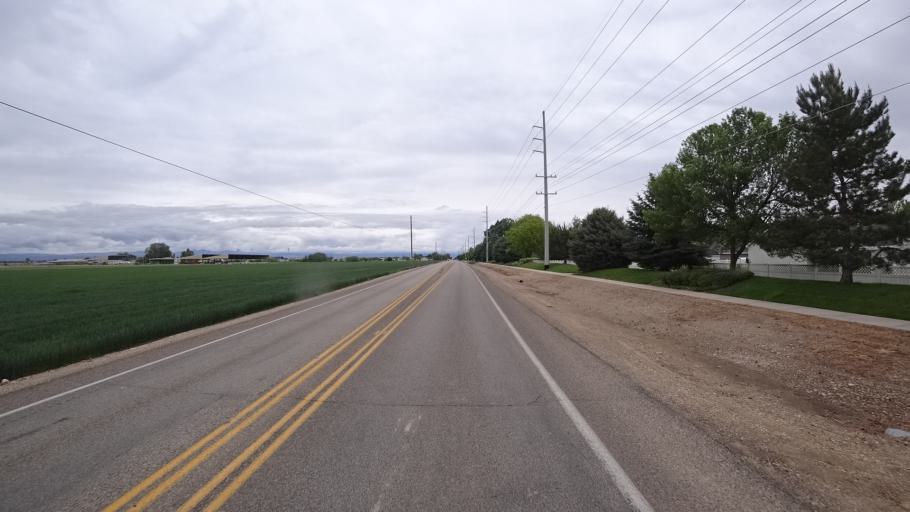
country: US
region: Idaho
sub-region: Ada County
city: Meridian
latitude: 43.6340
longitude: -116.4483
